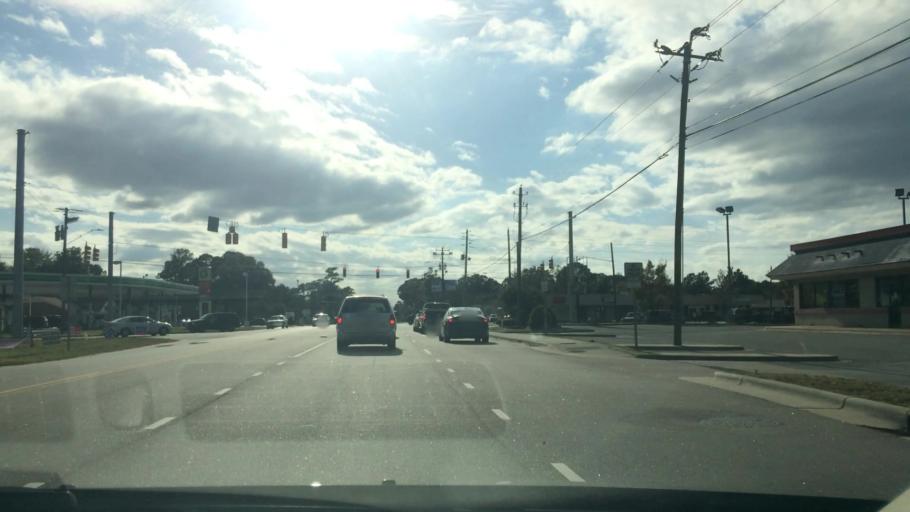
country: US
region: North Carolina
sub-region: Wayne County
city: Elroy
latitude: 35.3892
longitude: -77.9194
